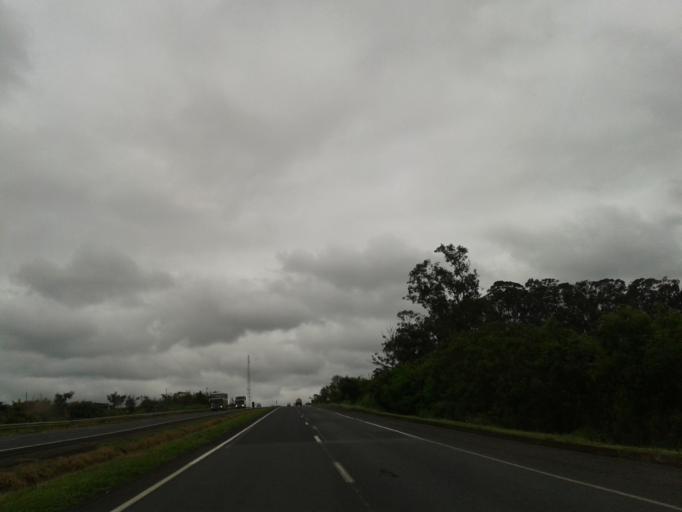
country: BR
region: Minas Gerais
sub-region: Uberlandia
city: Uberlandia
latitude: -18.9512
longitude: -48.2174
